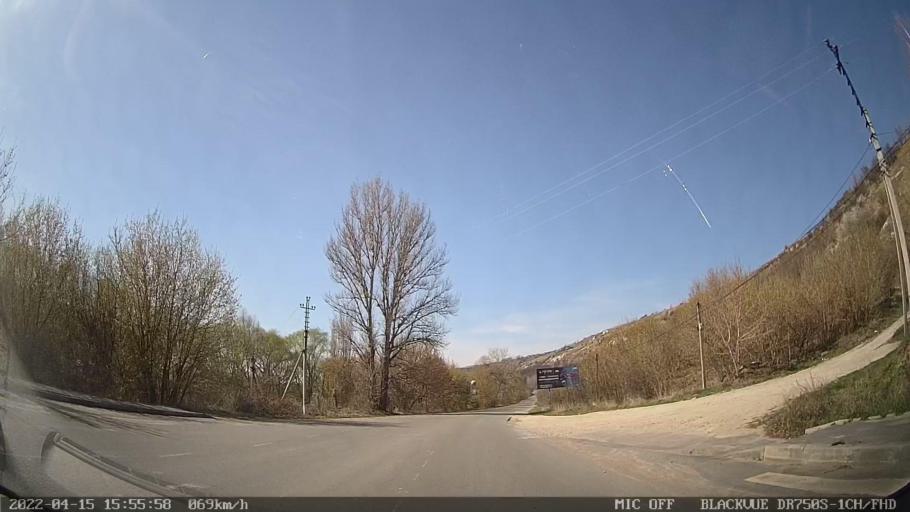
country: MD
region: Raionul Ocnita
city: Otaci
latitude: 48.4016
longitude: 27.8774
